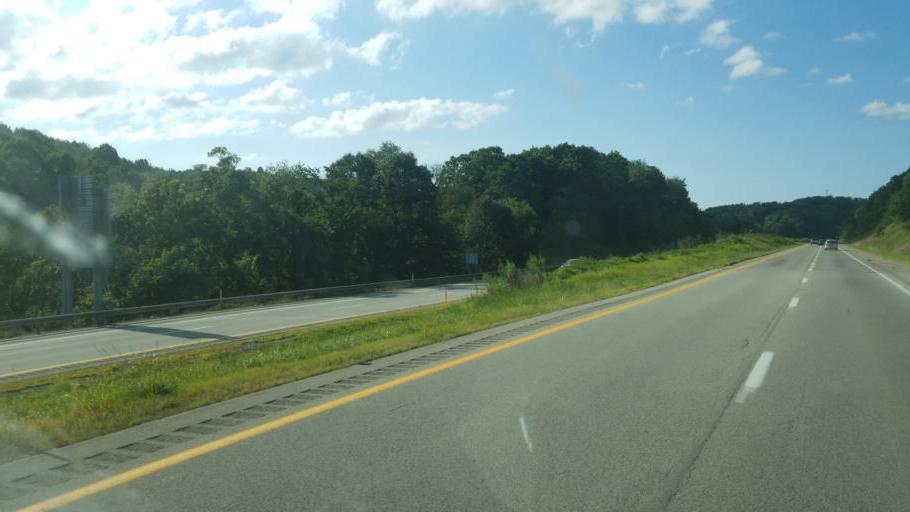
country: US
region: Pennsylvania
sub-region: Greene County
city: Waynesburg
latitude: 39.9917
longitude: -80.1853
